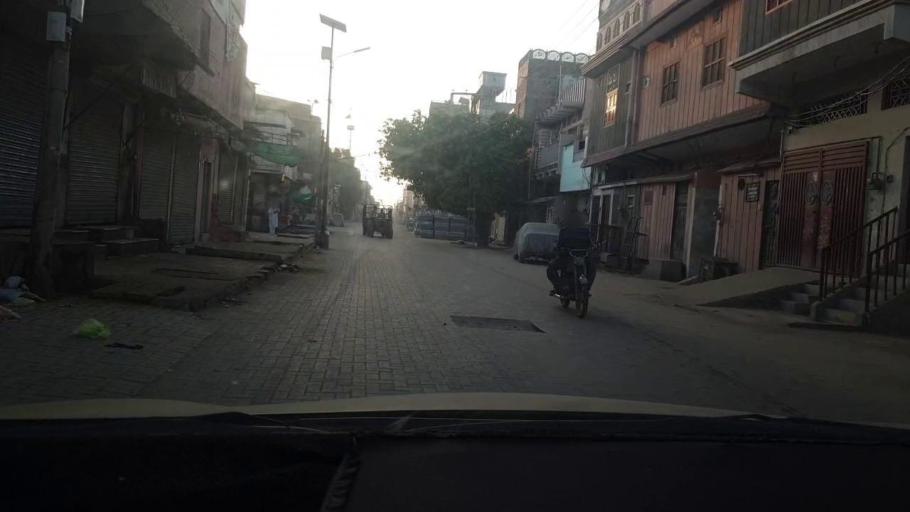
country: PK
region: Sindh
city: Larkana
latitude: 27.5509
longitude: 68.2154
